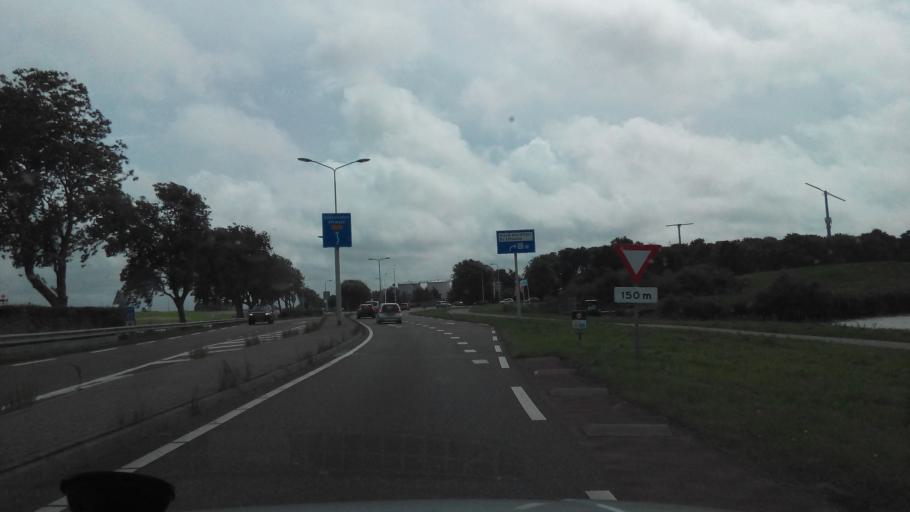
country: NL
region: North Holland
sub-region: Gemeente Den Helder
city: Den Helder
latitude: 52.9451
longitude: 4.7850
